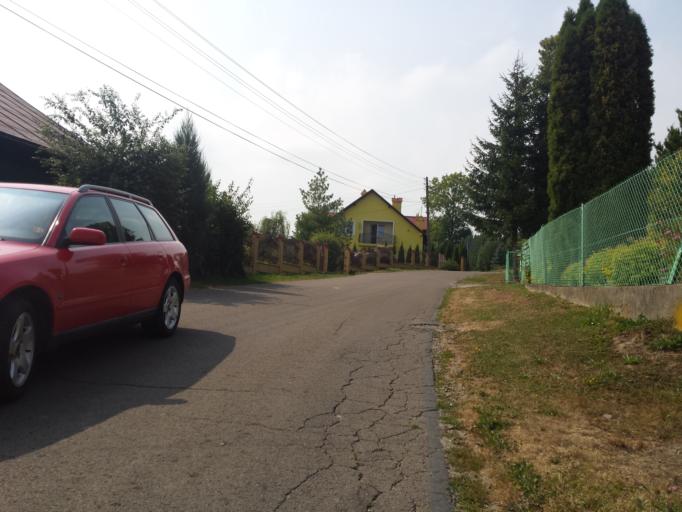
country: PL
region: Subcarpathian Voivodeship
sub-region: Powiat rzeszowski
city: Dynow
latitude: 49.8184
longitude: 22.2099
